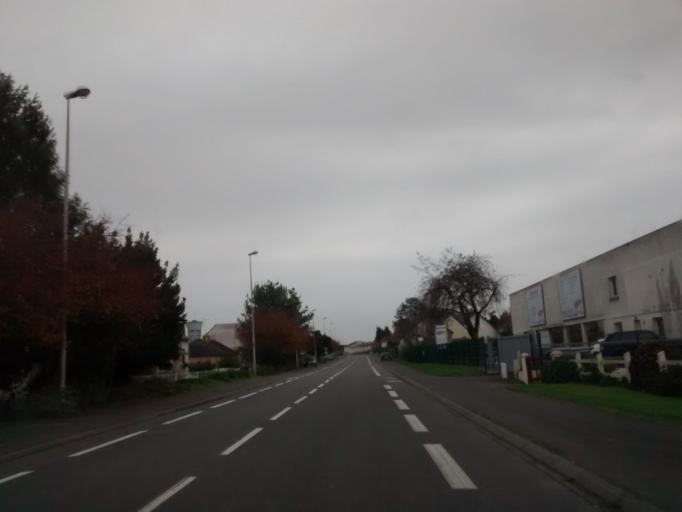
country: FR
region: Brittany
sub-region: Departement d'Ille-et-Vilaine
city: Noyal-sur-Vilaine
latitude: 48.1101
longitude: -1.5296
